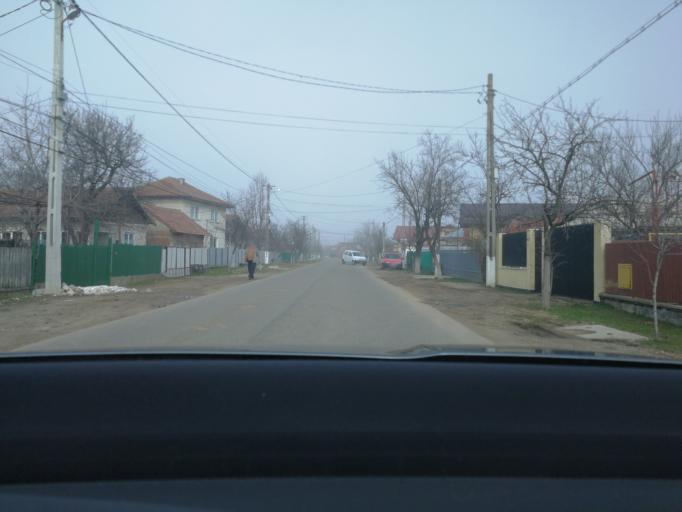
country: RO
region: Prahova
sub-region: Comuna Magureni
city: Lunca Prahovei
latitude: 45.0382
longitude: 25.7580
